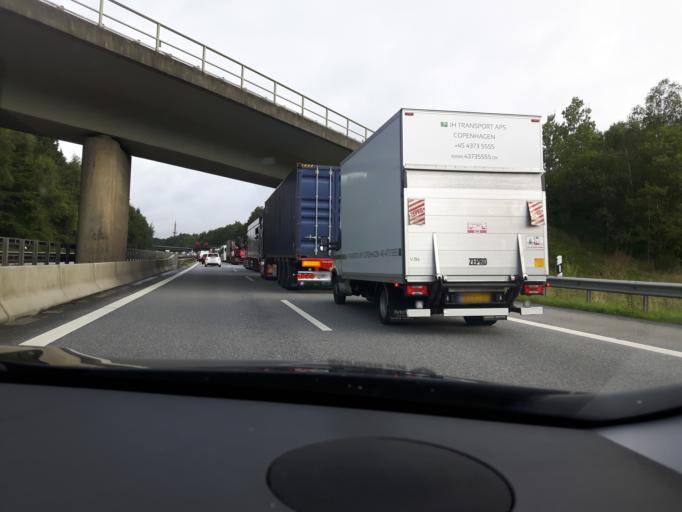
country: DE
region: Lower Saxony
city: Seevetal
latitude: 53.4265
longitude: 9.9281
